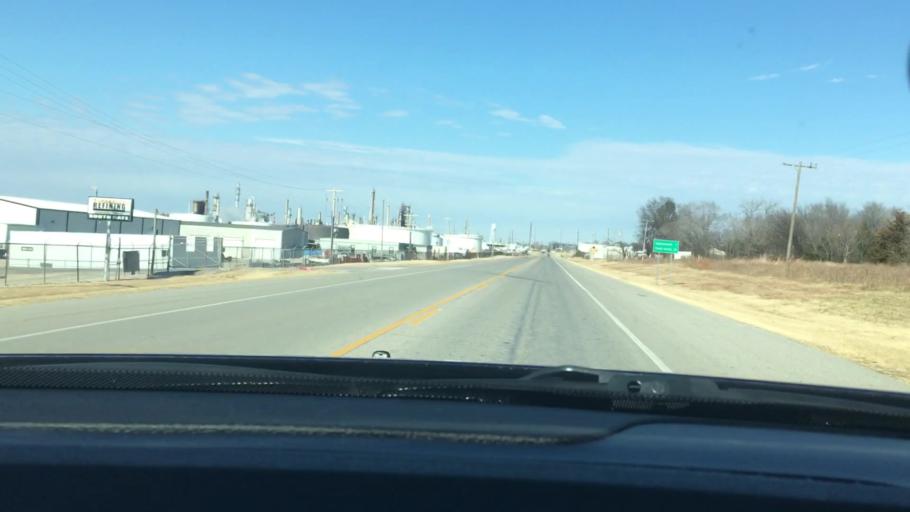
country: US
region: Oklahoma
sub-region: Garvin County
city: Wynnewood
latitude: 34.6244
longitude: -97.1631
